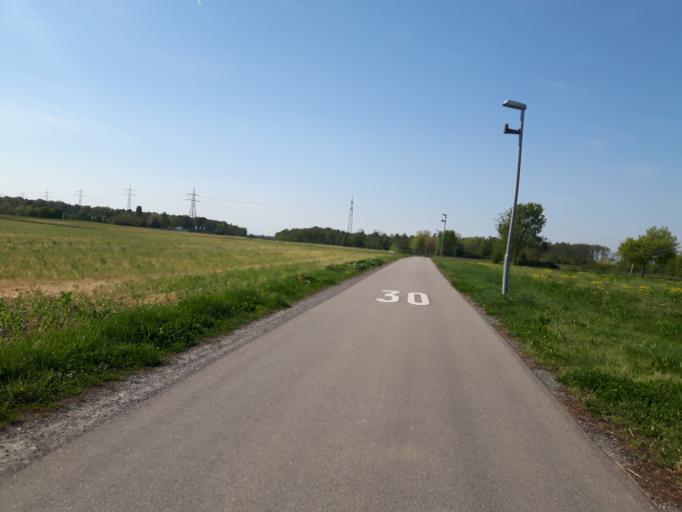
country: DE
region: Baden-Wuerttemberg
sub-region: Karlsruhe Region
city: Reilingen
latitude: 49.2791
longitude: 8.5886
